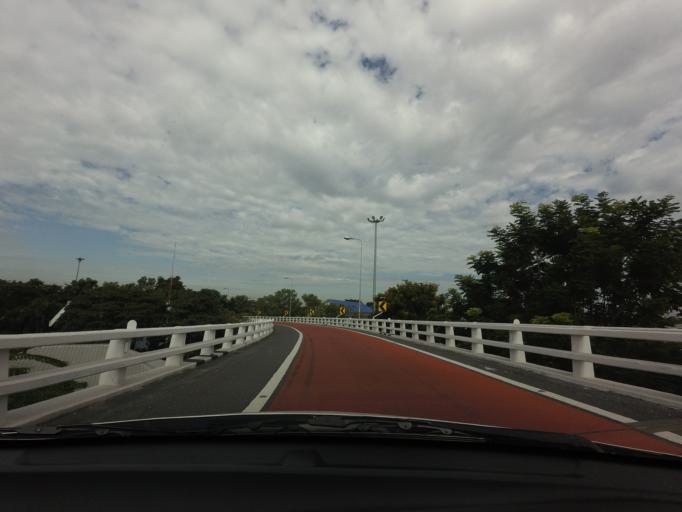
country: TH
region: Pathum Thani
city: Thanyaburi
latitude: 14.0082
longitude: 100.7043
